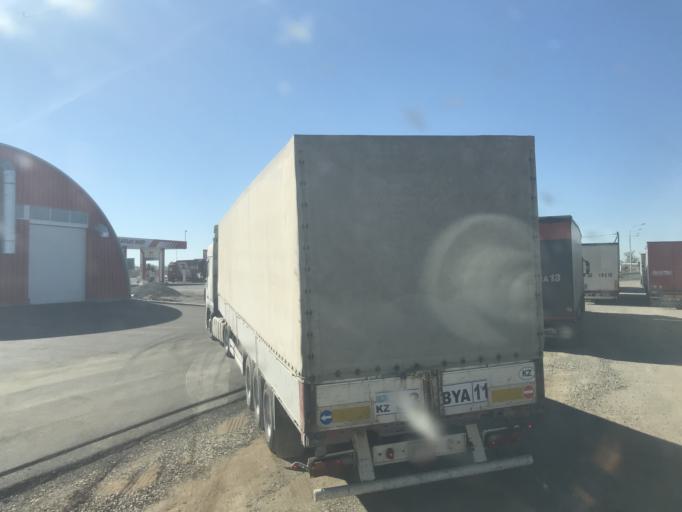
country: KZ
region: Aqtoebe
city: Aqtobe
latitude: 50.2963
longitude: 57.4764
